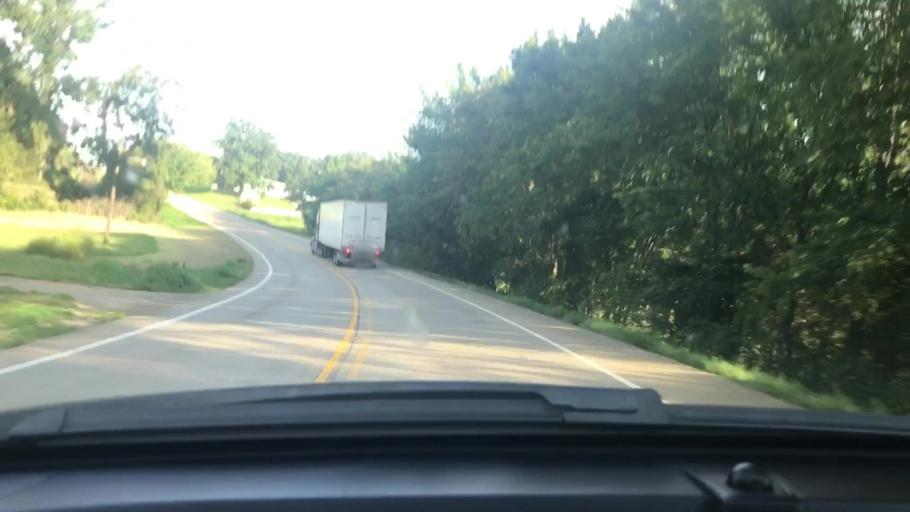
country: US
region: Arkansas
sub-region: Sharp County
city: Cherokee Village
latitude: 36.2403
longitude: -91.2646
